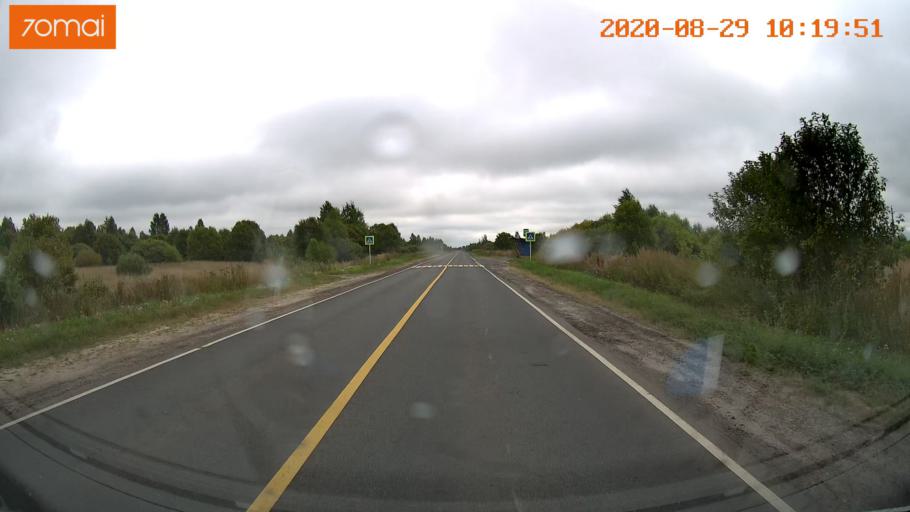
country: RU
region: Ivanovo
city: Yur'yevets
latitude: 57.3263
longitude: 42.8694
